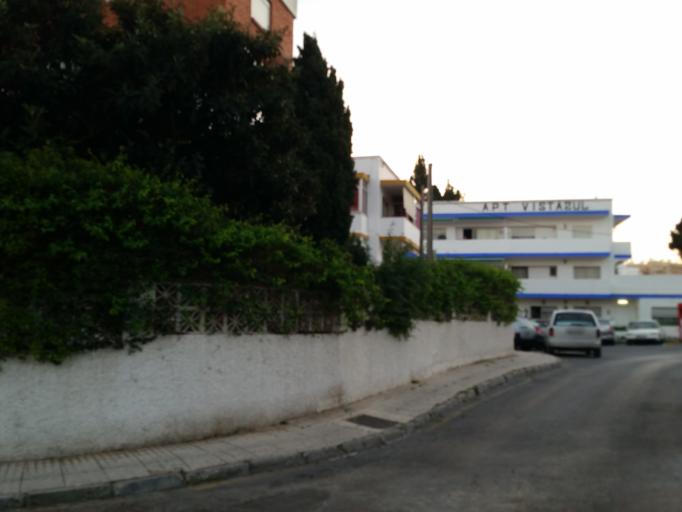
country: ES
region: Andalusia
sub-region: Provincia de Malaga
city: Torremolinos
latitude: 36.6018
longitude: -4.5230
